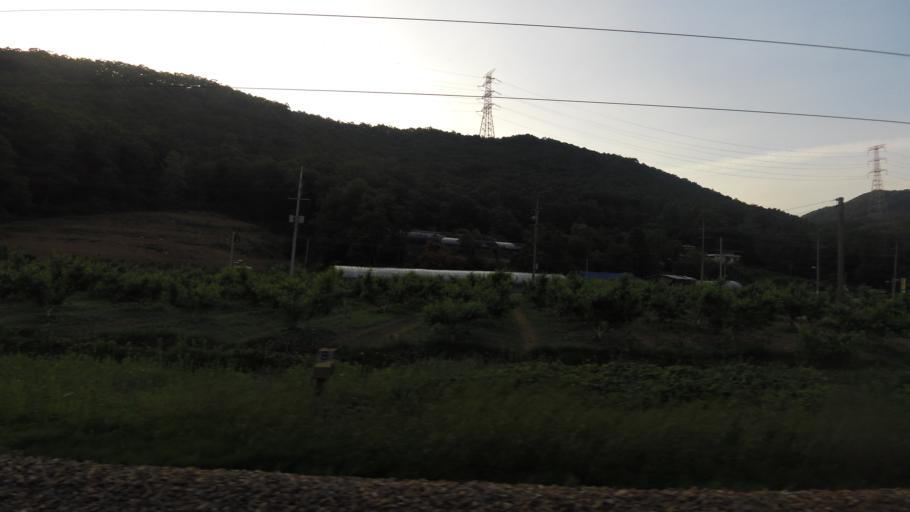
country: KR
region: Chungcheongnam-do
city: Cheonan
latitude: 36.6610
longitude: 127.2328
